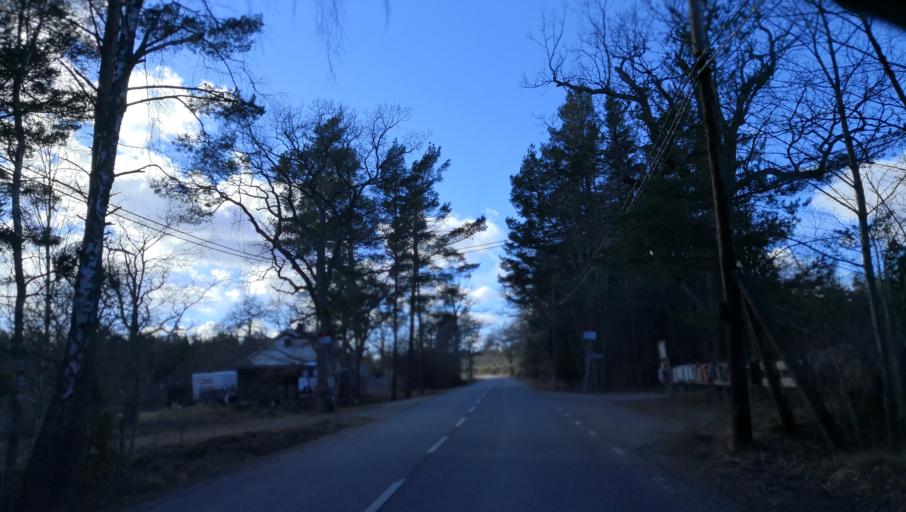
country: SE
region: Stockholm
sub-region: Varmdo Kommun
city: Holo
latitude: 59.3557
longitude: 18.6157
